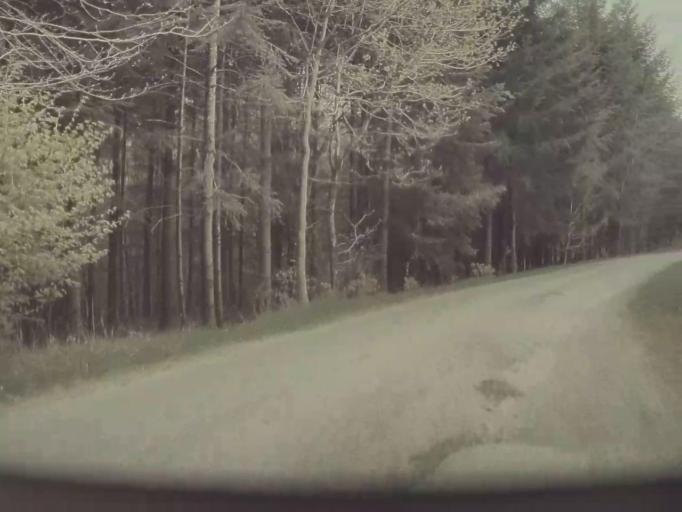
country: BE
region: Wallonia
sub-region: Province du Luxembourg
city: La Roche-en-Ardenne
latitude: 50.2403
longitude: 5.5974
